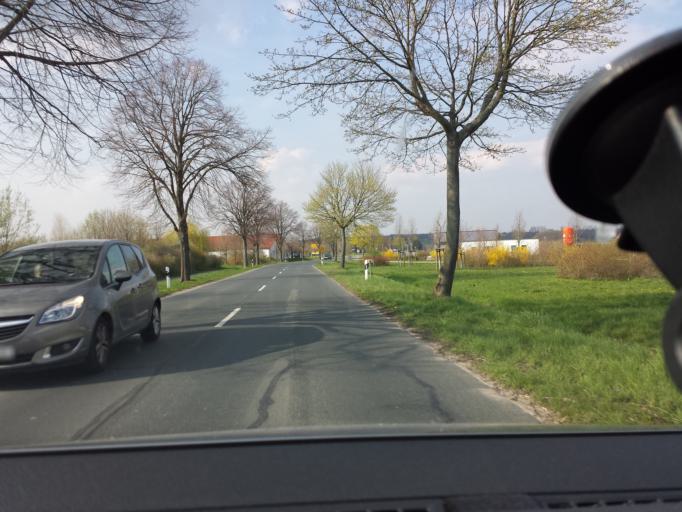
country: DE
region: Lower Saxony
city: Braunschweig
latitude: 52.2641
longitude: 10.4486
